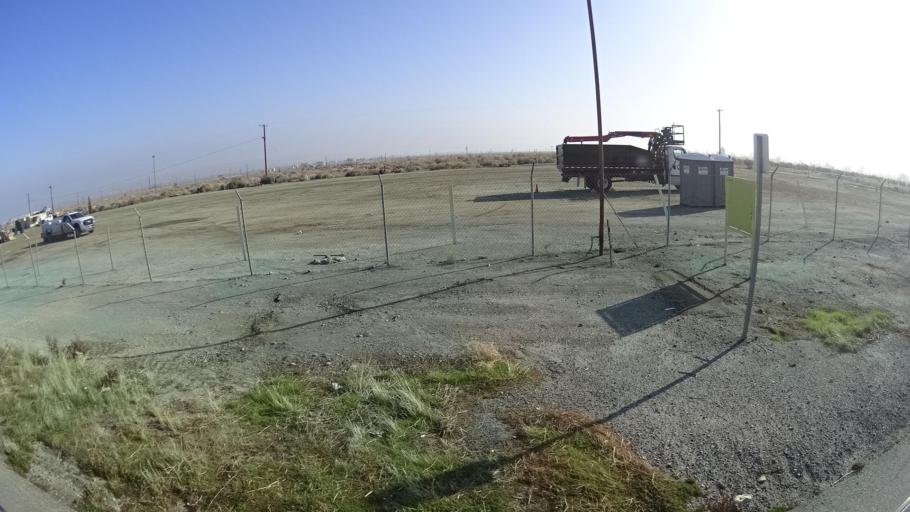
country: US
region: California
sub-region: Kern County
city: Taft Heights
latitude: 35.1832
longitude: -119.5503
